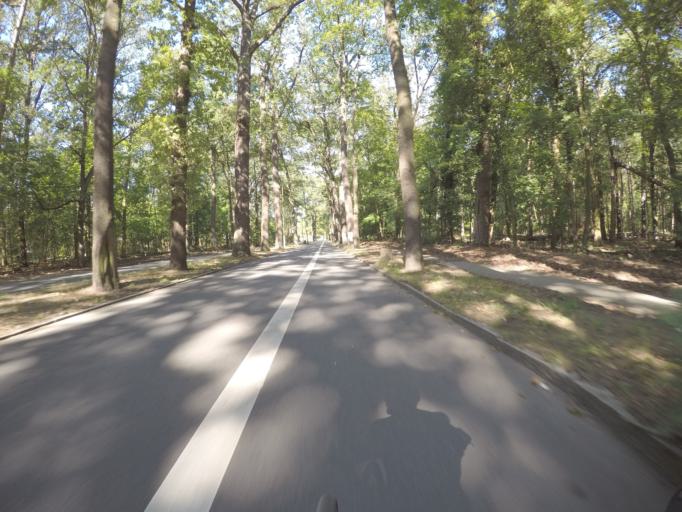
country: DE
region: Berlin
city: Konradshohe
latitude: 52.5798
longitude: 13.2280
